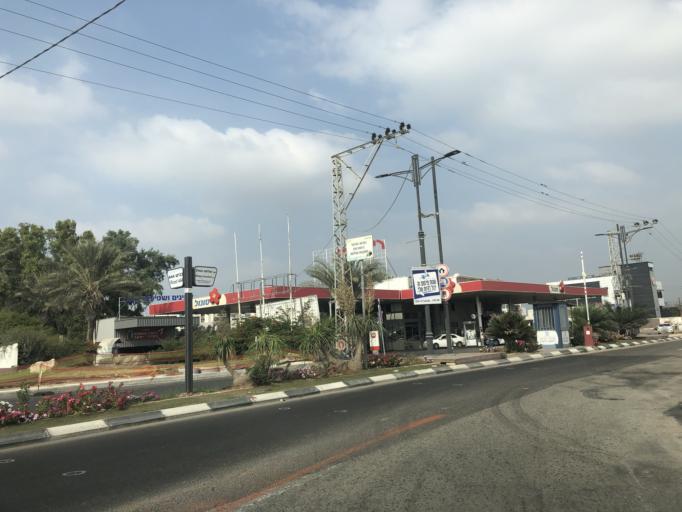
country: IL
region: Central District
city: Rosh Ha'Ayin
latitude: 32.0930
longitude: 34.9407
